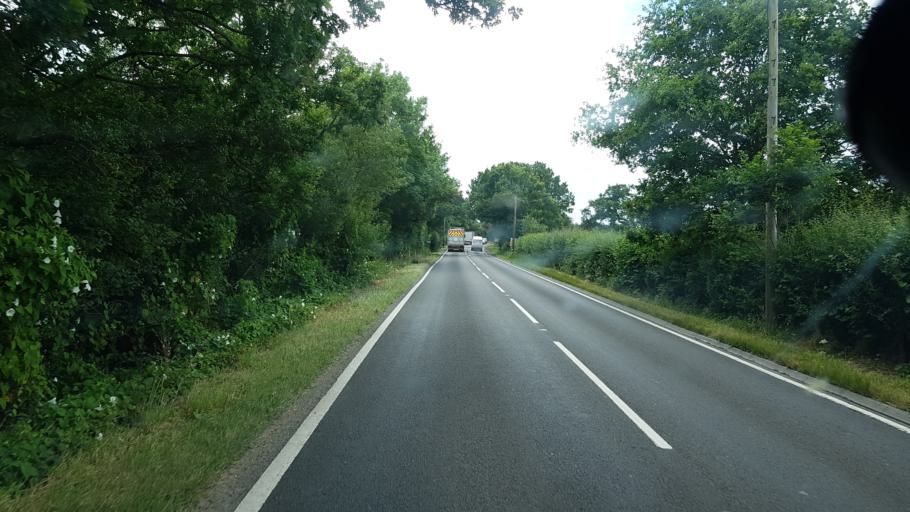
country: GB
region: England
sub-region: Surrey
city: Felbridge
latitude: 51.1727
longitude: -0.0498
